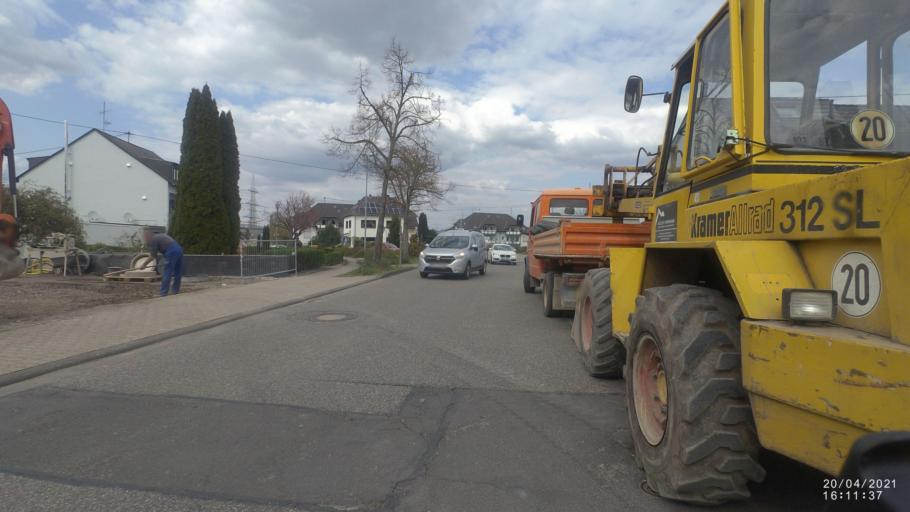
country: DE
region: Rheinland-Pfalz
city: Kettig
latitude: 50.3995
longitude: 7.4628
